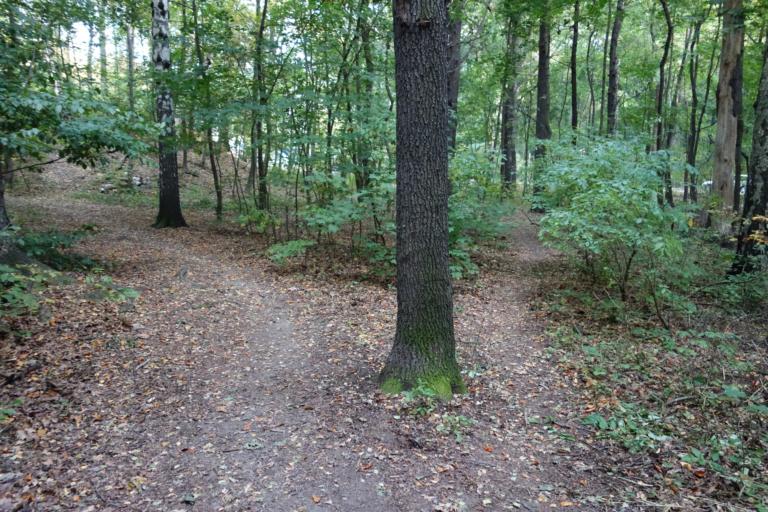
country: DE
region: Saxony
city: Hilbersdorf
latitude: 50.8547
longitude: 12.9583
